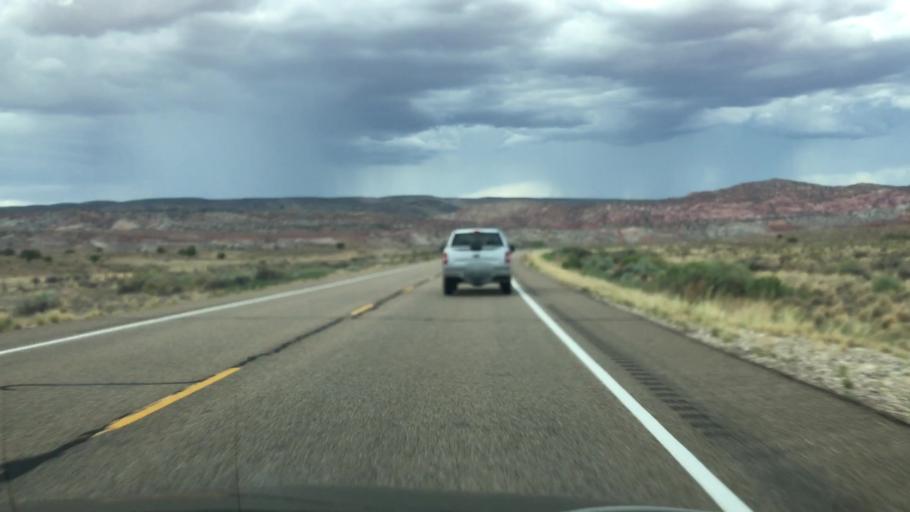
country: US
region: Arizona
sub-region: Coconino County
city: Page
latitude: 37.1117
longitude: -111.9283
